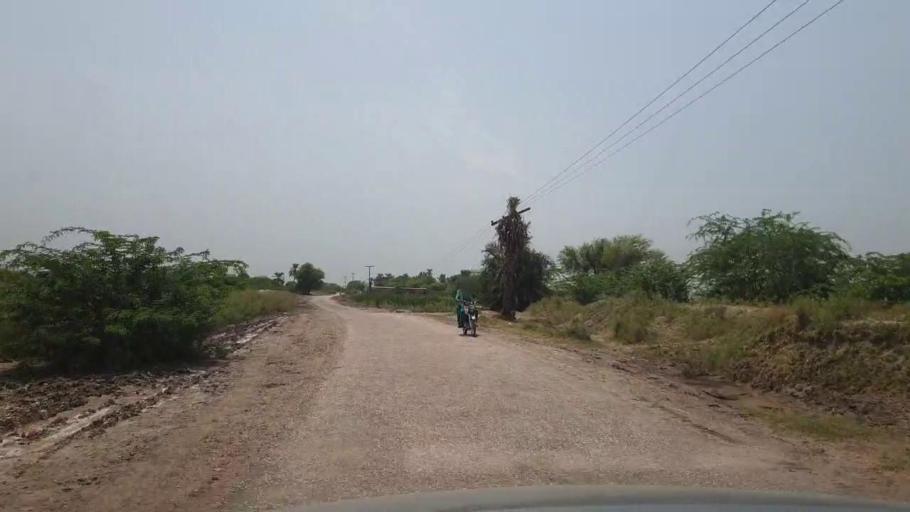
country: PK
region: Sindh
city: Garhi Yasin
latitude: 27.8806
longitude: 68.4952
